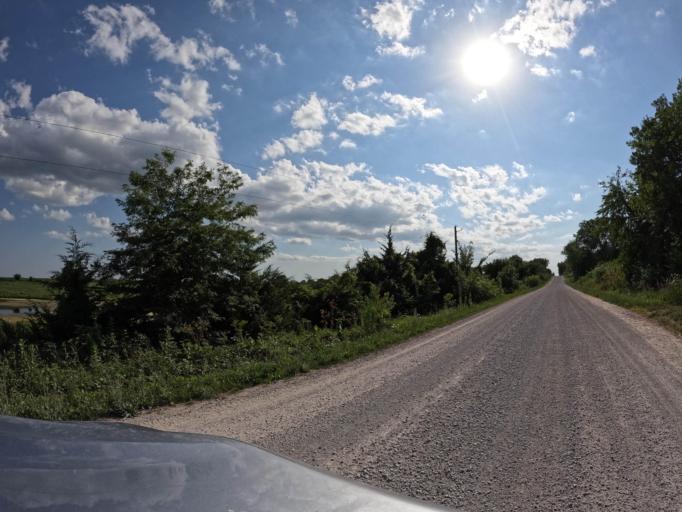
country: US
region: Iowa
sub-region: Appanoose County
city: Centerville
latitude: 40.7178
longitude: -93.0253
